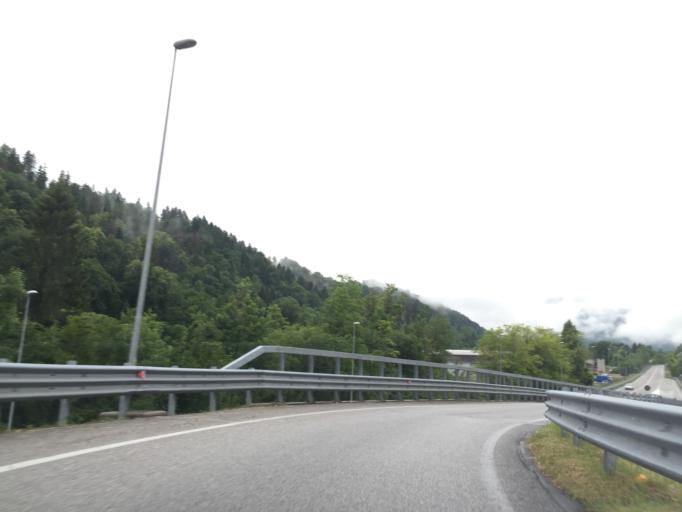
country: IT
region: Veneto
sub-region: Provincia di Belluno
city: Feltre
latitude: 46.0098
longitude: 11.8853
